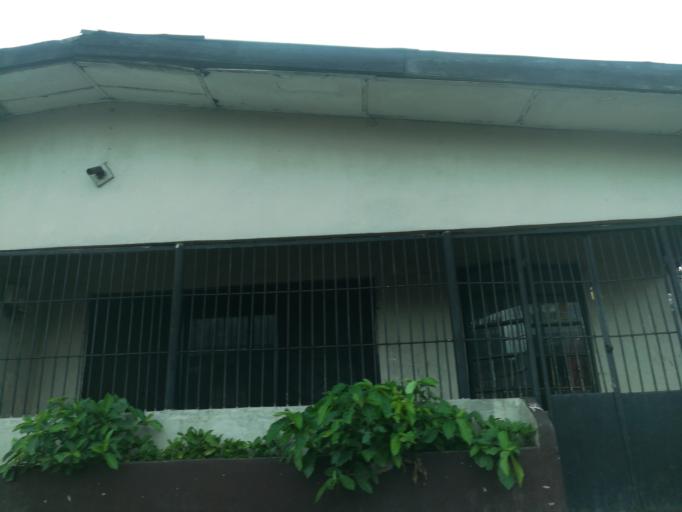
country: NG
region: Rivers
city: Port Harcourt
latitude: 4.8178
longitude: 7.0102
